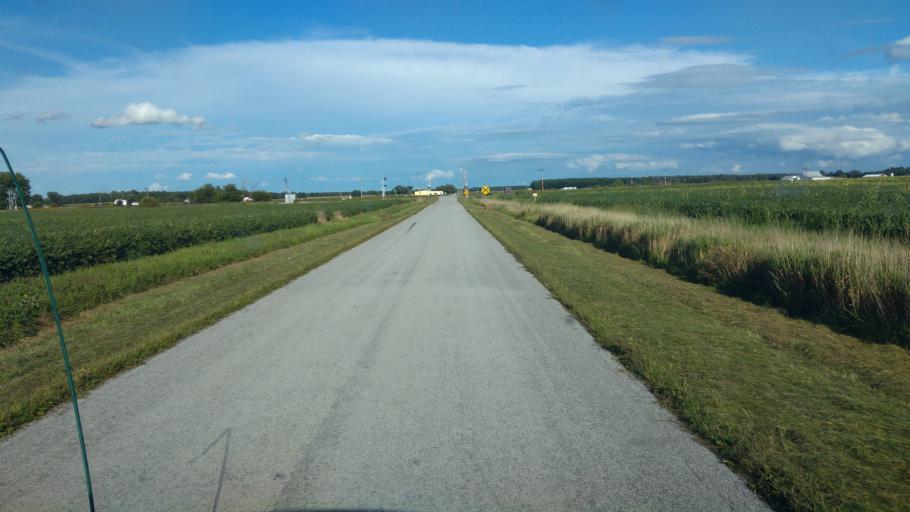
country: US
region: Ohio
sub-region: Hardin County
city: Kenton
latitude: 40.7612
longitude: -83.6456
